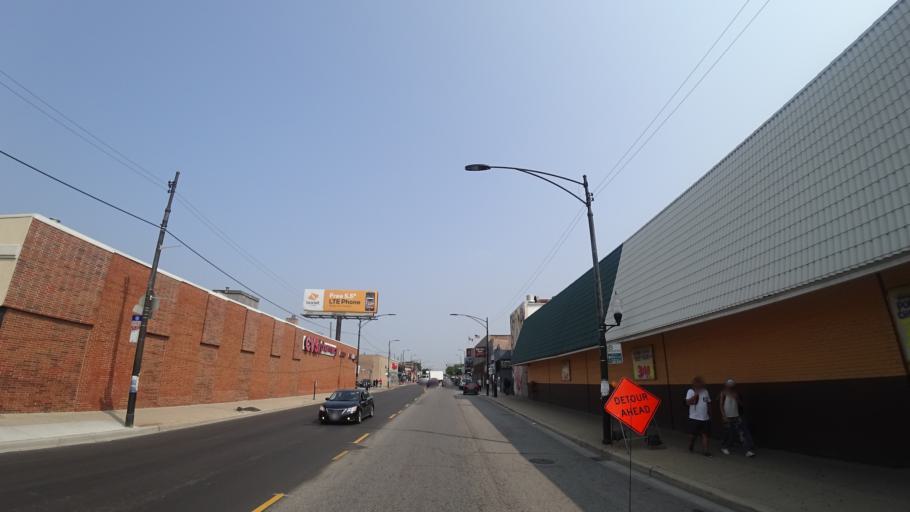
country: US
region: Illinois
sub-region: Cook County
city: Cicero
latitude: 41.8432
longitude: -87.7245
